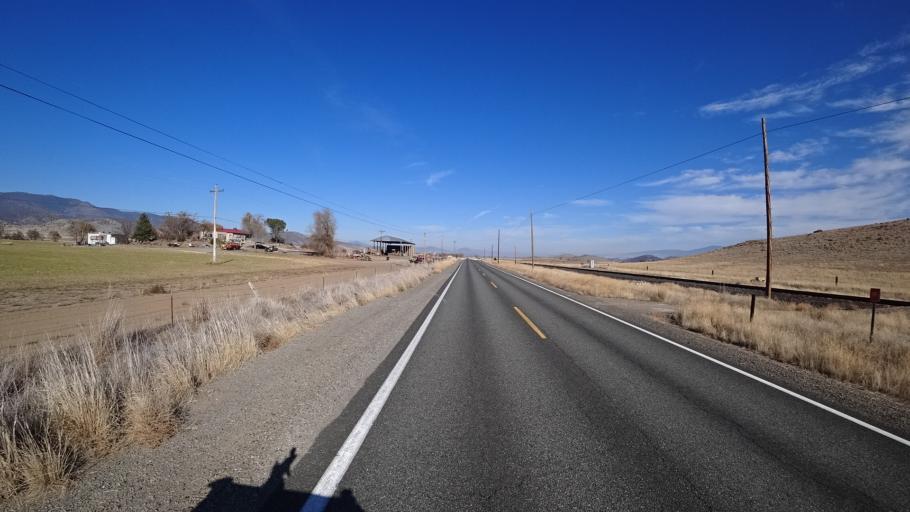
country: US
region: California
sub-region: Siskiyou County
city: Montague
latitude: 41.5537
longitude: -122.5262
